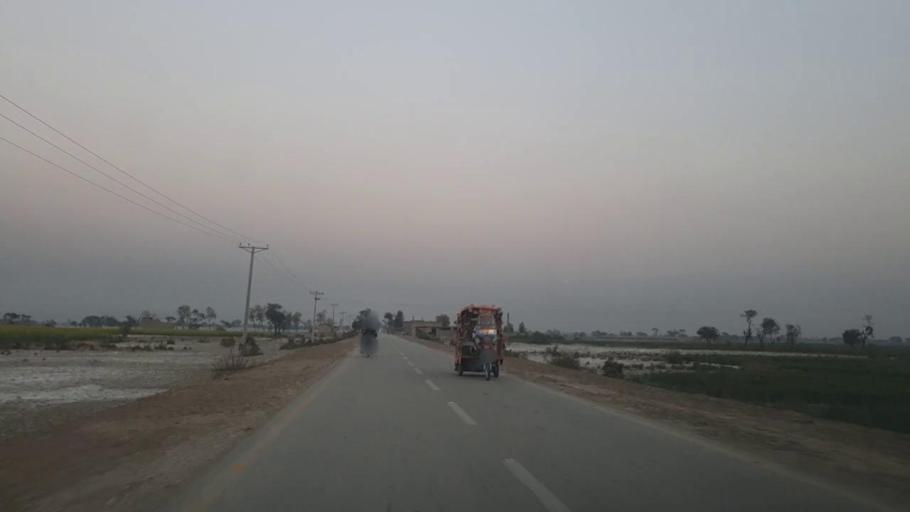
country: PK
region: Sindh
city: Naushahro Firoz
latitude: 26.8488
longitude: 68.0515
